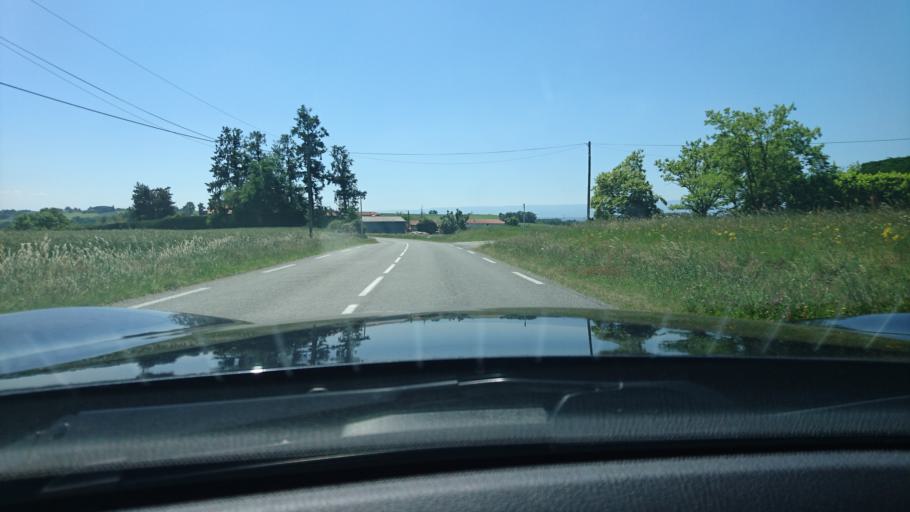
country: FR
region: Rhone-Alpes
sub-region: Departement de la Loire
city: Rozier-en-Donzy
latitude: 45.7849
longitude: 4.2819
